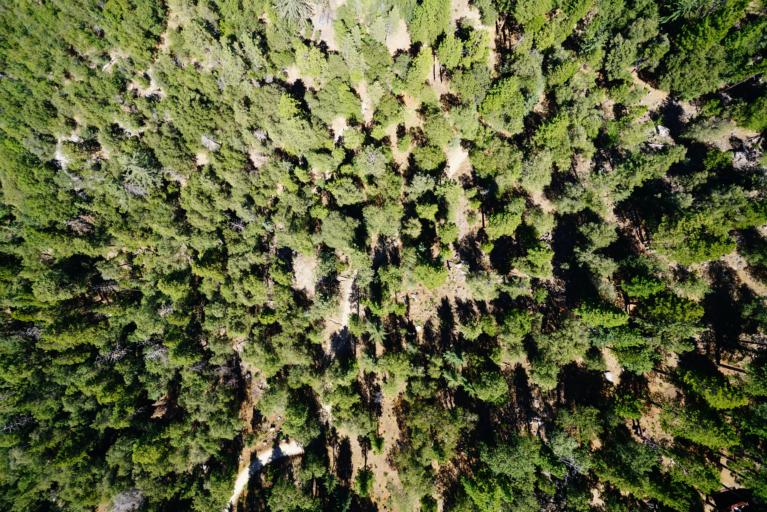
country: US
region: California
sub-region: Riverside County
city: Idyllwild-Pine Cove
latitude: 33.7603
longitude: -116.7480
